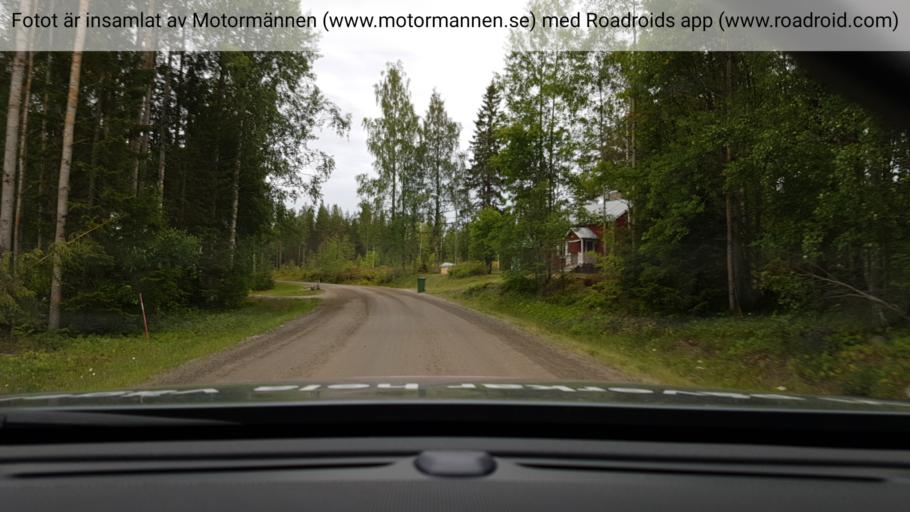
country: SE
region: Vaesterbotten
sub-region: Vannas Kommun
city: Vannasby
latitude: 64.0917
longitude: 20.0433
